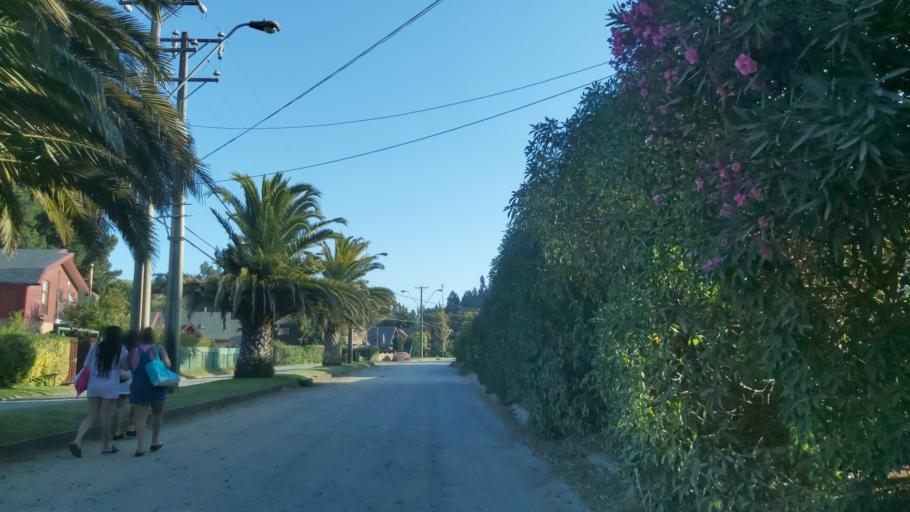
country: CL
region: Biobio
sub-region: Provincia de Concepcion
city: Tome
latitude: -36.5324
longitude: -72.9303
